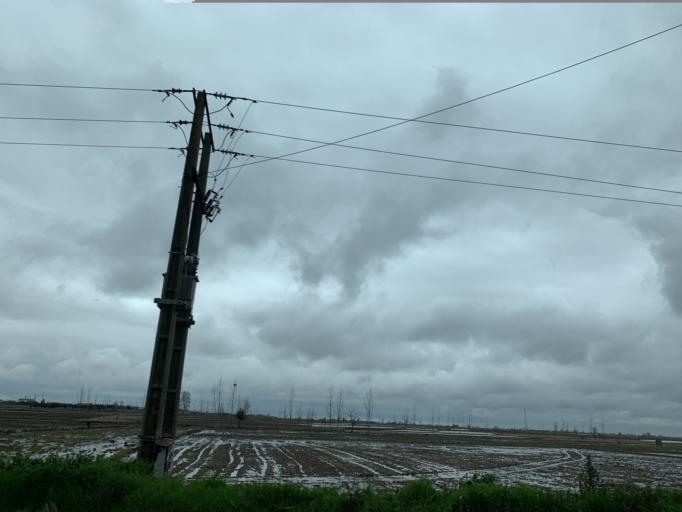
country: IR
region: Mazandaran
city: Amol
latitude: 36.4802
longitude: 52.4665
